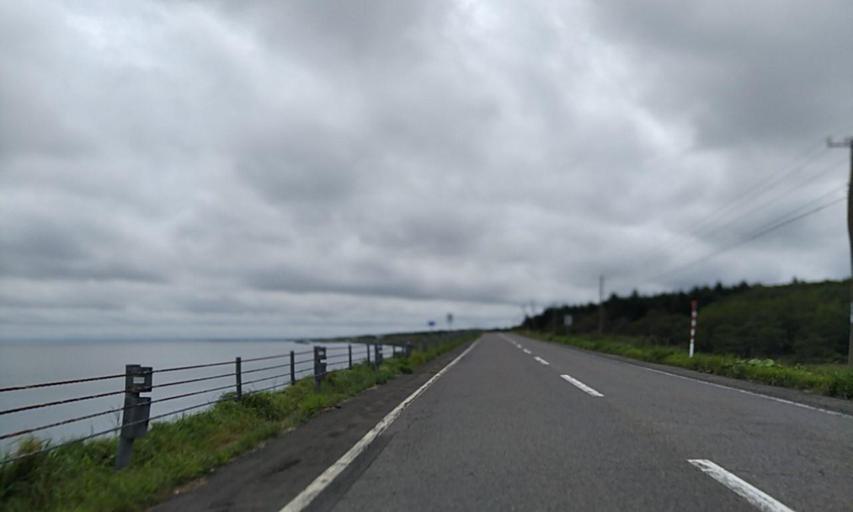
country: JP
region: Hokkaido
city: Shibetsu
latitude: 43.4414
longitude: 145.2620
